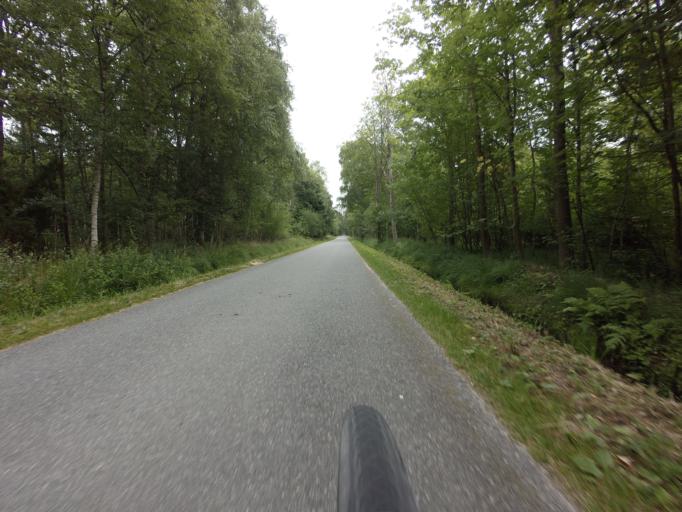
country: DK
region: North Denmark
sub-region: Laeso Kommune
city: Byrum
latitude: 57.2895
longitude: 10.9816
